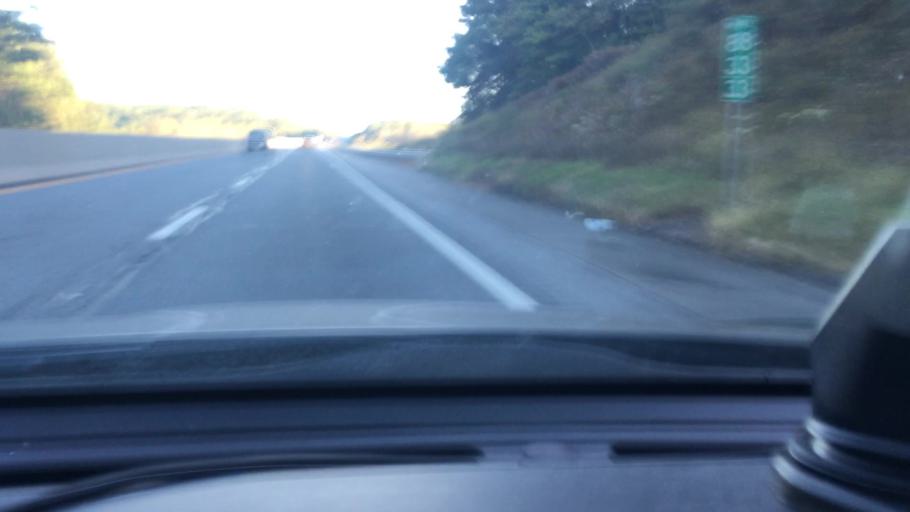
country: US
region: Pennsylvania
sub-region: Carbon County
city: Towamensing Trails
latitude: 40.9306
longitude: -75.6437
